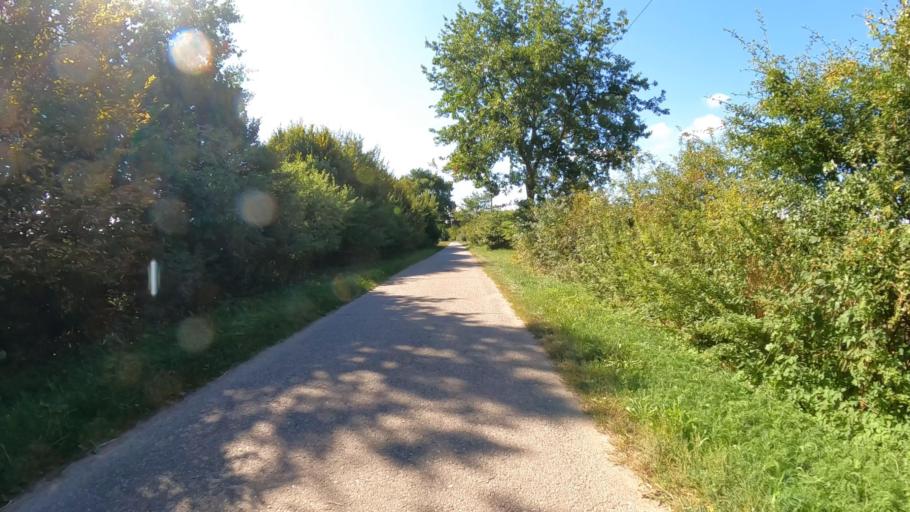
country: DE
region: Schleswig-Holstein
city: Gross Schenkenberg
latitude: 53.8029
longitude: 10.5735
